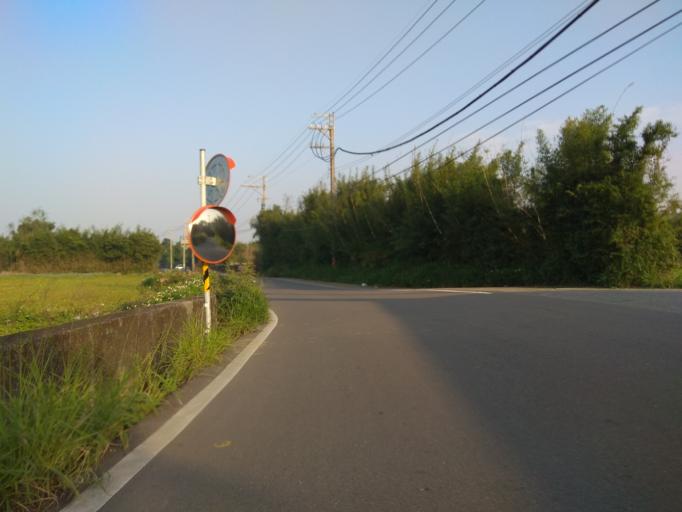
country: TW
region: Taiwan
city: Daxi
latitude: 24.9071
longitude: 121.1915
